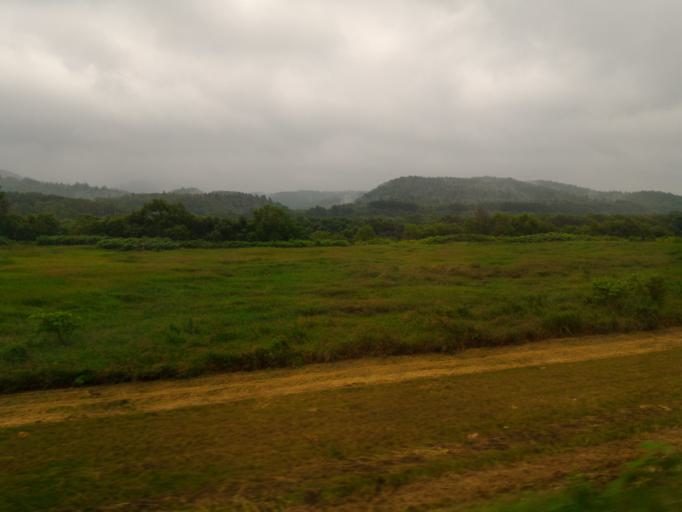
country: JP
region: Hokkaido
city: Nayoro
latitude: 44.7622
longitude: 142.0527
